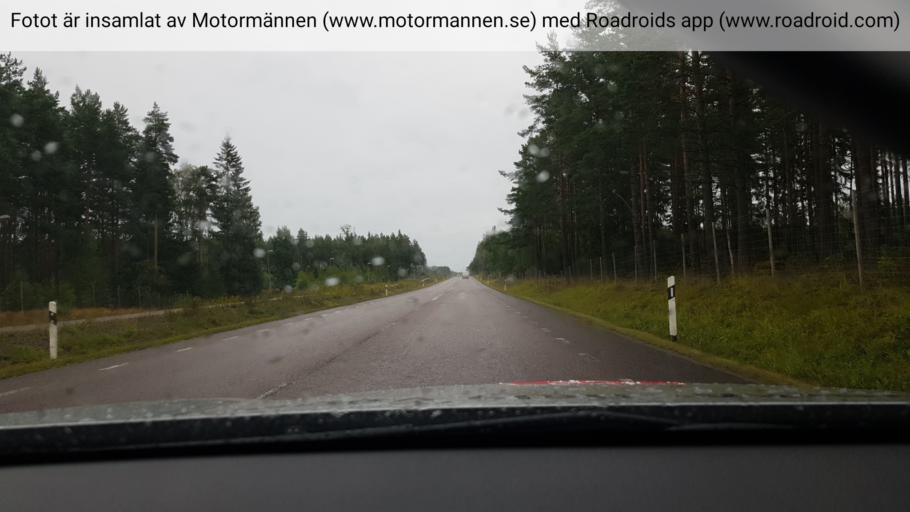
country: SE
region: Uppsala
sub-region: Alvkarleby Kommun
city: Skutskaer
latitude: 60.6468
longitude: 17.2813
